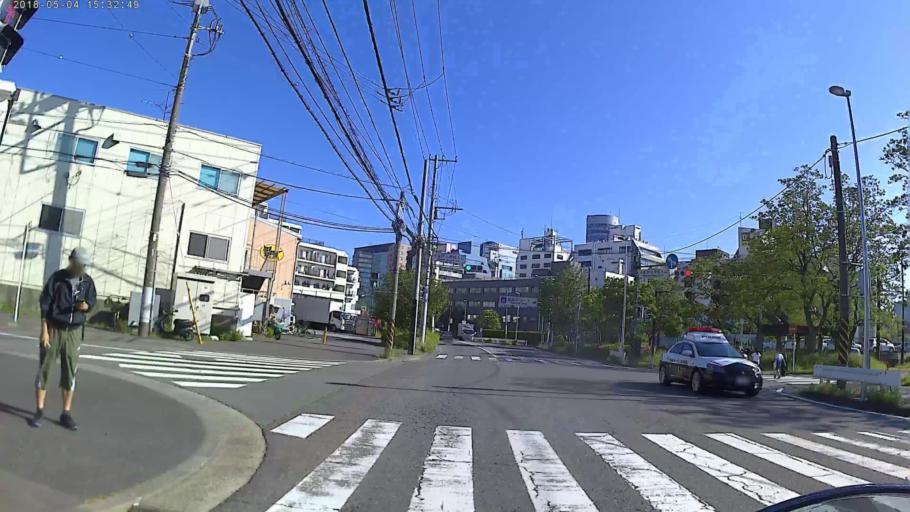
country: JP
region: Kanagawa
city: Yokohama
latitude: 35.5157
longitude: 139.6208
